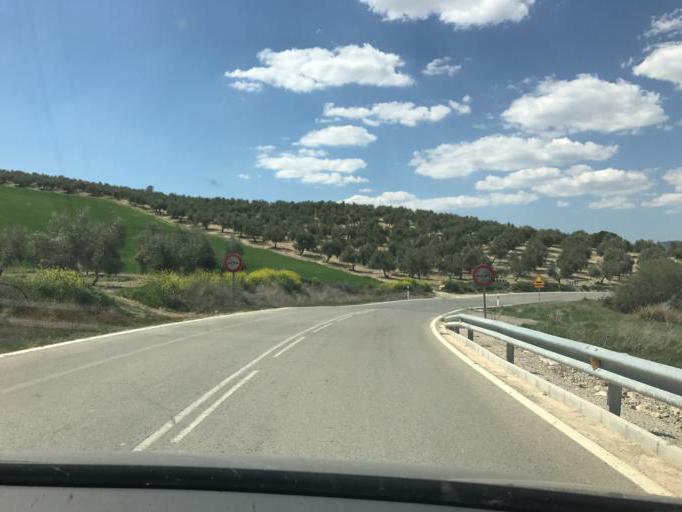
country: ES
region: Andalusia
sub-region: Provincia de Granada
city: Campotejar
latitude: 37.4457
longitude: -3.6122
